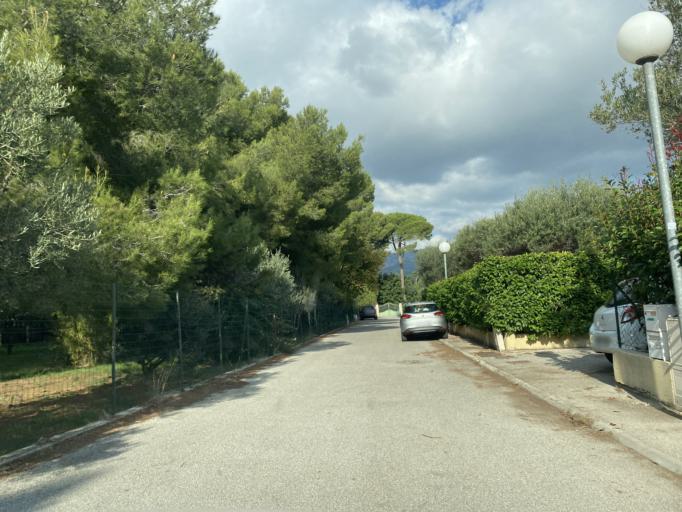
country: FR
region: Provence-Alpes-Cote d'Azur
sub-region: Departement du Var
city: La Seyne-sur-Mer
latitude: 43.1210
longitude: 5.8825
